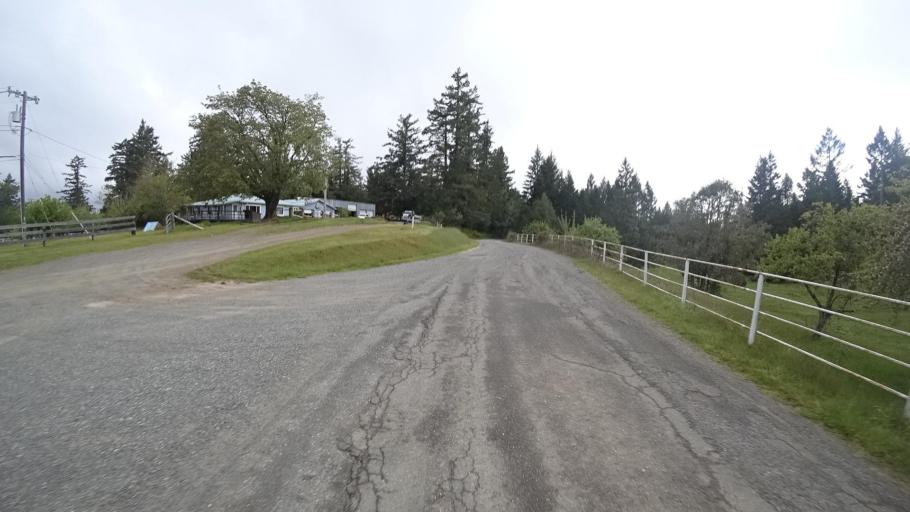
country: US
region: California
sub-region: Humboldt County
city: Redway
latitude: 40.2328
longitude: -123.7619
